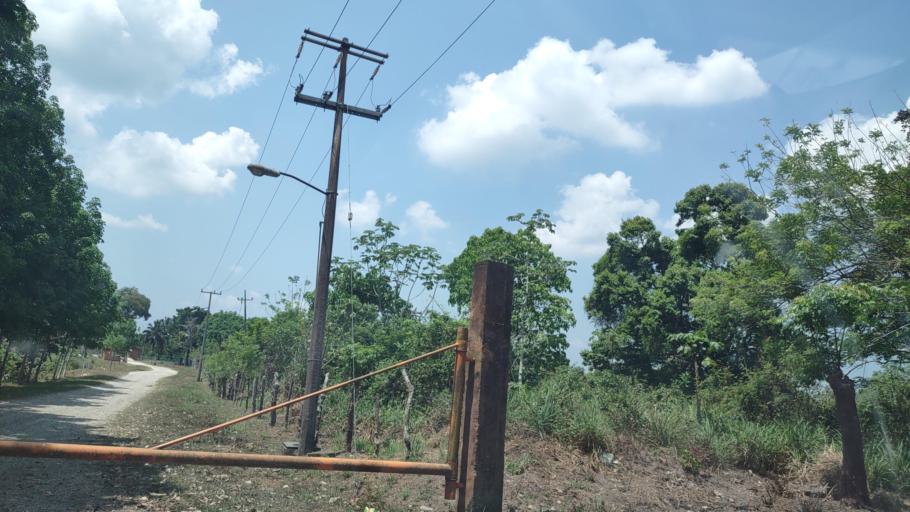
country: MX
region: Veracruz
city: Las Choapas
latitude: 17.9318
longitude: -94.1538
